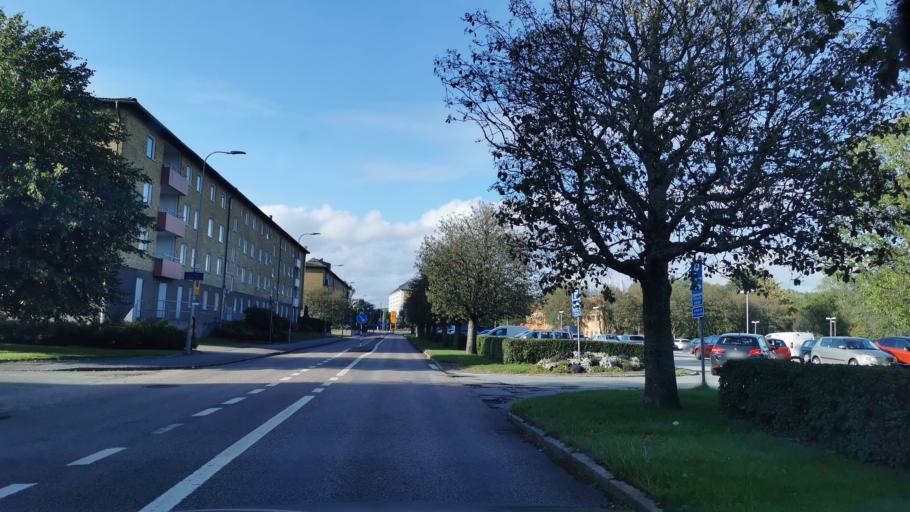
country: SE
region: Vaestra Goetaland
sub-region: Goteborg
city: Majorna
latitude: 57.6656
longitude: 11.9351
